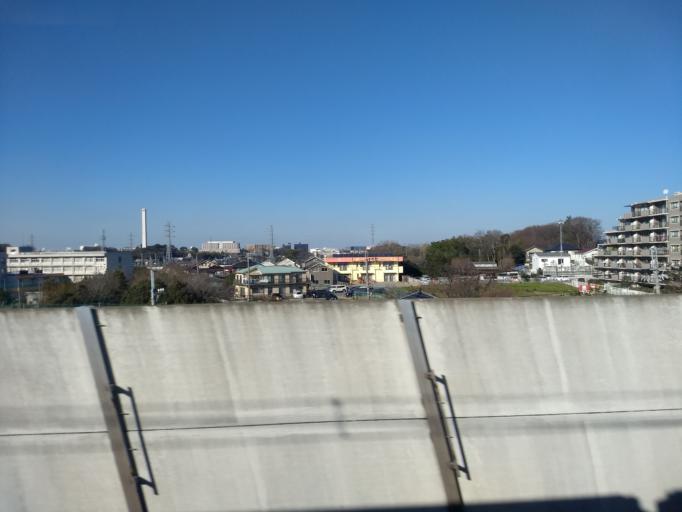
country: JP
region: Chiba
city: Matsudo
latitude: 35.7647
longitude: 139.9257
